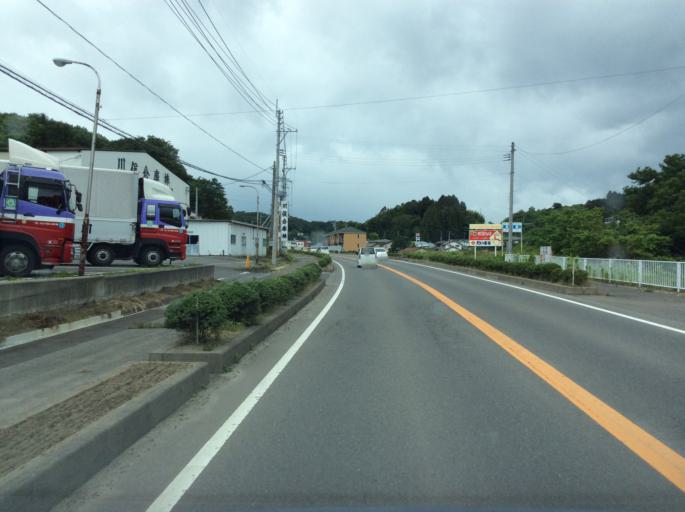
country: JP
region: Fukushima
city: Fukushima-shi
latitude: 37.6662
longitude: 140.5865
